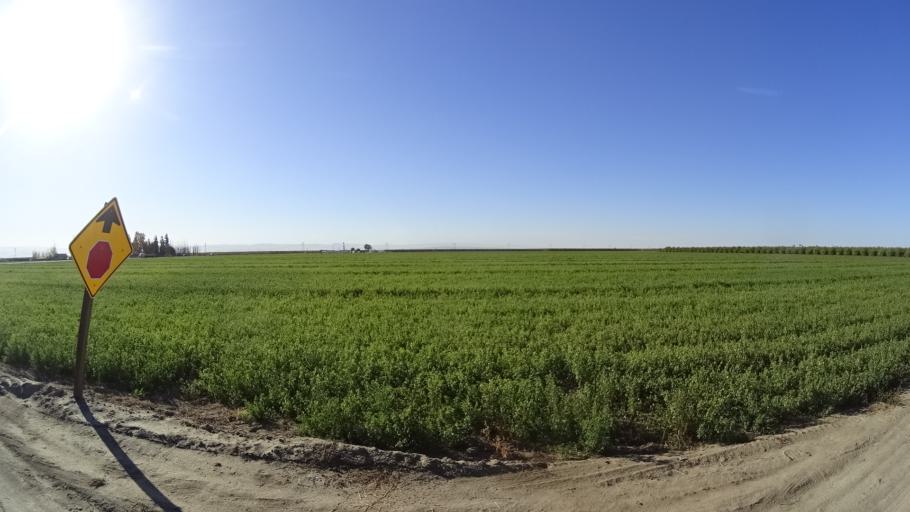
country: US
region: California
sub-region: Kern County
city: Greenacres
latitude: 35.2690
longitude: -119.1183
